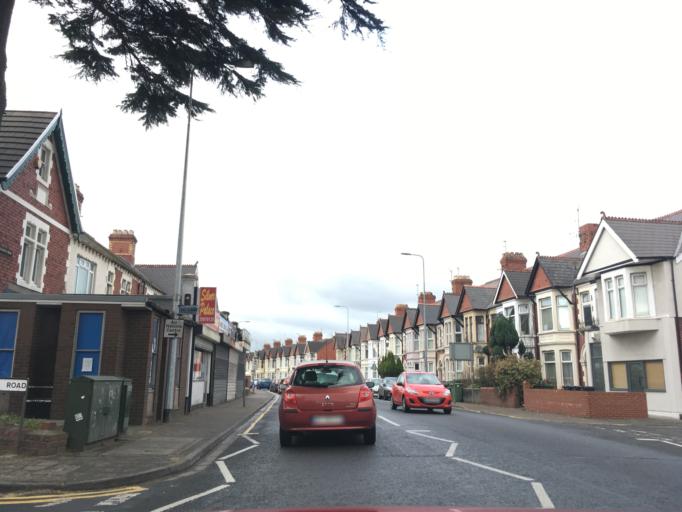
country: GB
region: Wales
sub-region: Cardiff
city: Cardiff
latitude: 51.5034
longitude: -3.1920
